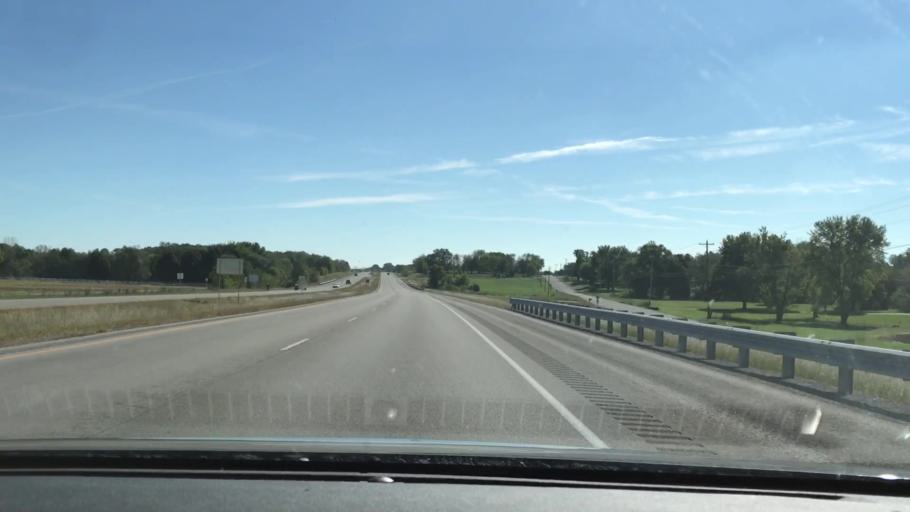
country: US
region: Kentucky
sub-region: Christian County
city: Hopkinsville
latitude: 36.8563
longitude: -87.4209
